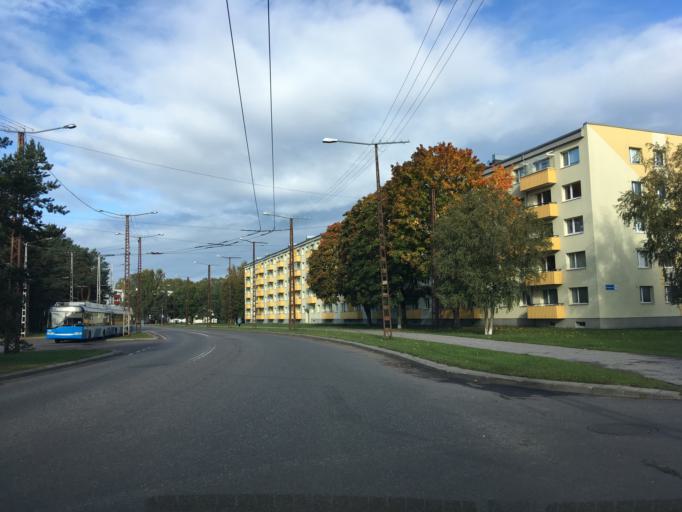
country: EE
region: Harju
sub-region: Tallinna linn
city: Tallinn
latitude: 59.3998
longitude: 24.6805
